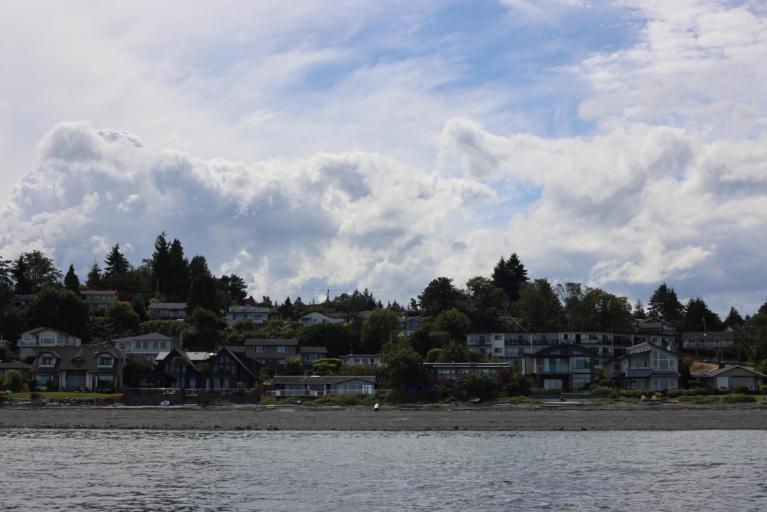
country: CA
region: British Columbia
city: Nanaimo
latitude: 49.2030
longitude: -123.9670
